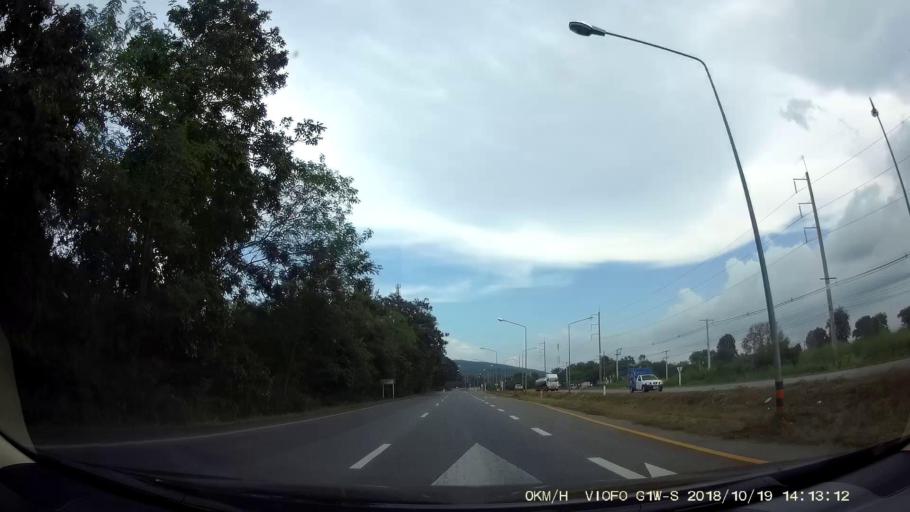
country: TH
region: Chaiyaphum
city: Khon Sawan
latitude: 15.9586
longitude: 102.1791
